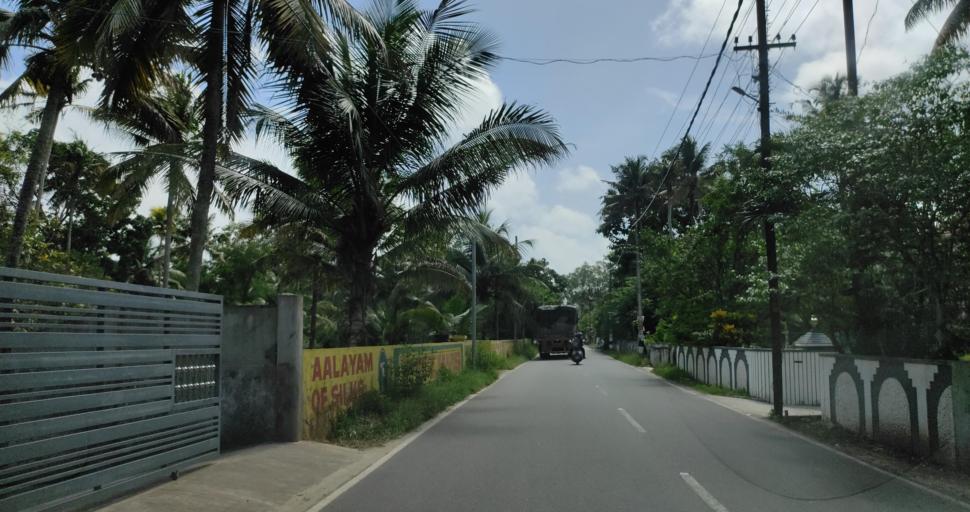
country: IN
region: Kerala
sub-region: Alappuzha
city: Shertallai
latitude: 9.6543
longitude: 76.3447
